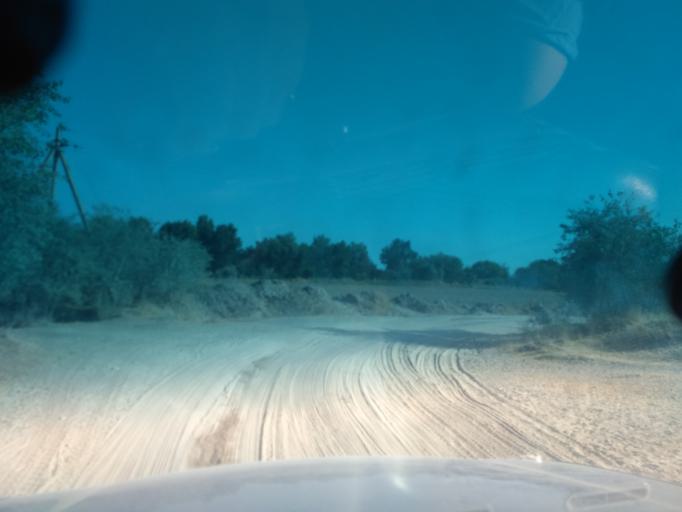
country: TJ
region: Viloyati Sughd
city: Buston
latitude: 40.5560
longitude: 69.0754
